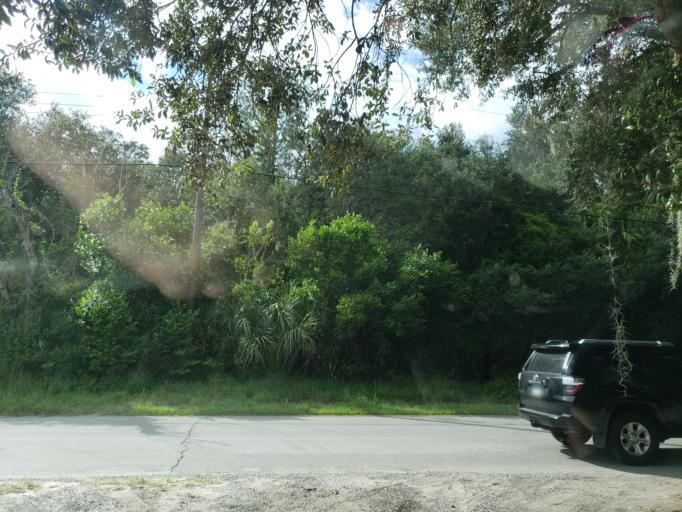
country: US
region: Florida
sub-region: Hillsborough County
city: Fish Hawk
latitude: 27.8510
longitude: -82.1702
